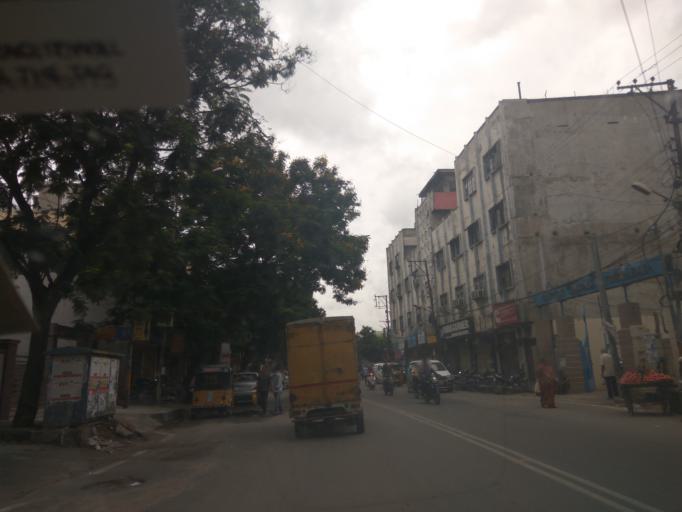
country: IN
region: Telangana
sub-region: Hyderabad
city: Hyderabad
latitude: 17.3956
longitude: 78.4896
